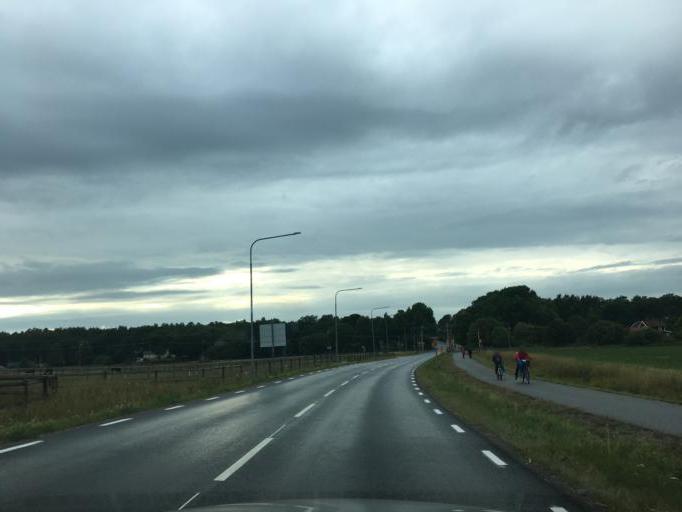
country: SE
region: Vaestmanland
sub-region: Hallstahammars Kommun
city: Kolback
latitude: 59.5266
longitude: 16.2462
